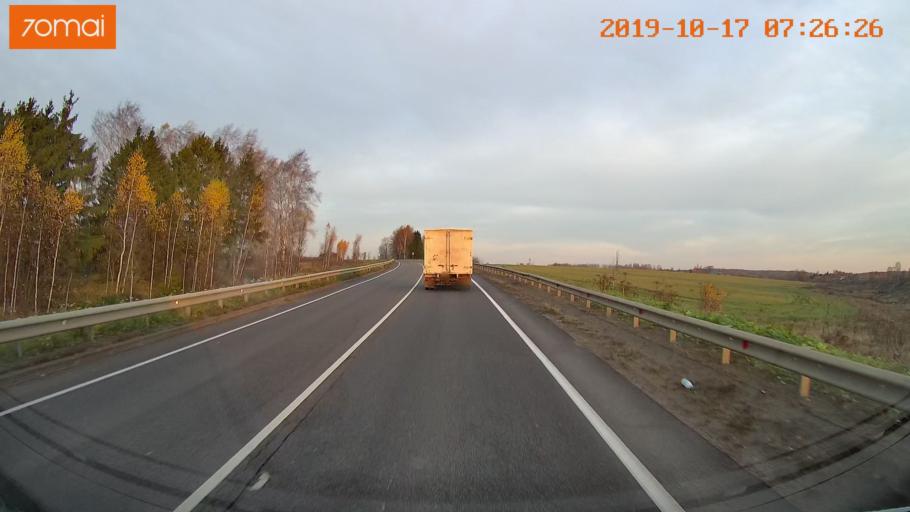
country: RU
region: Ivanovo
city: Gavrilov Posad
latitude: 56.3573
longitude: 40.0924
